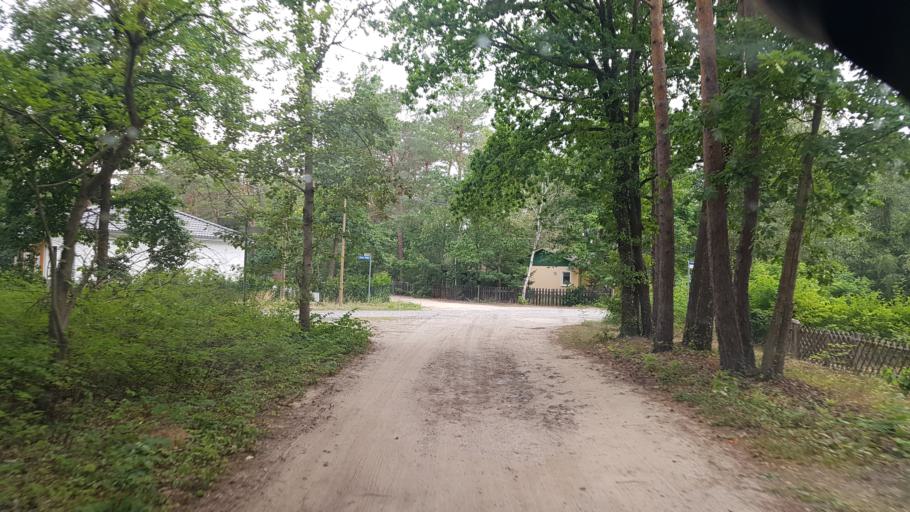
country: DE
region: Brandenburg
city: Gross Koris
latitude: 52.1615
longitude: 13.6939
